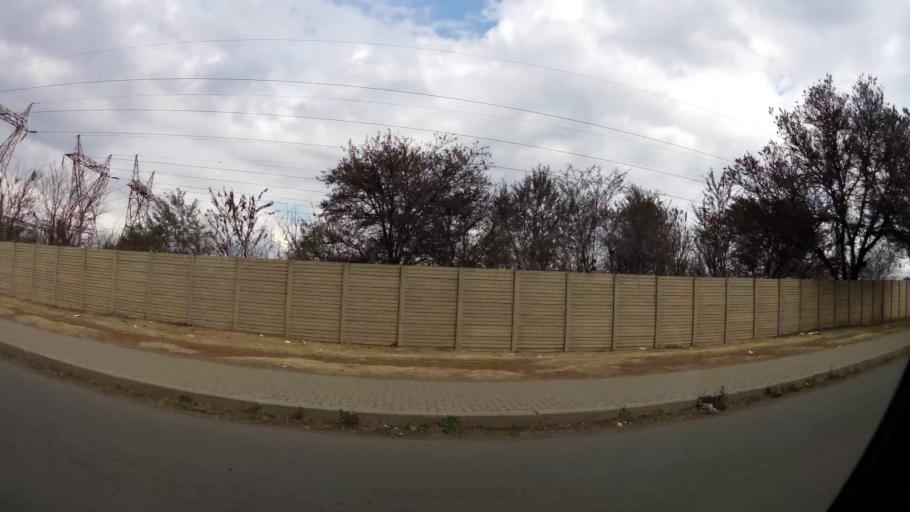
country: ZA
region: Gauteng
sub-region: Sedibeng District Municipality
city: Vanderbijlpark
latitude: -26.6902
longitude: 27.8077
